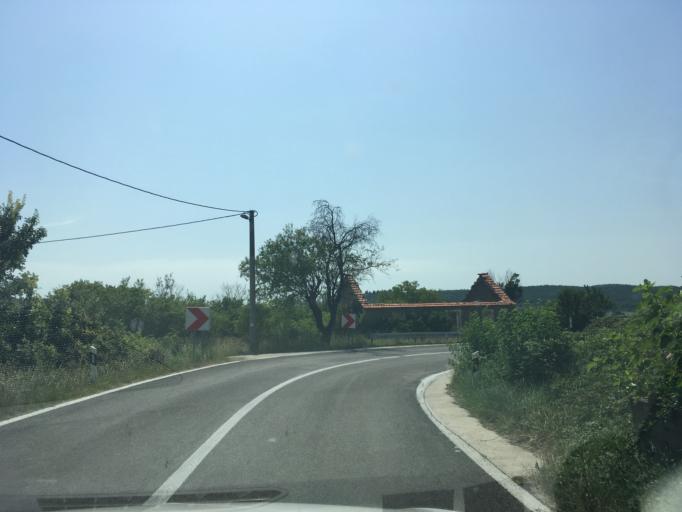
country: HR
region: Sibensko-Kniniska
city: Zaton
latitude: 43.9306
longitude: 15.8301
